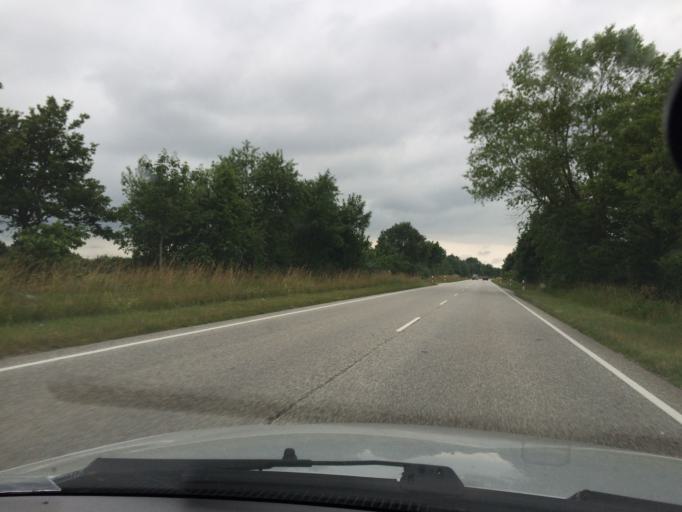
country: DE
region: Schleswig-Holstein
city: Oeversee
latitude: 54.6800
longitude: 9.4357
